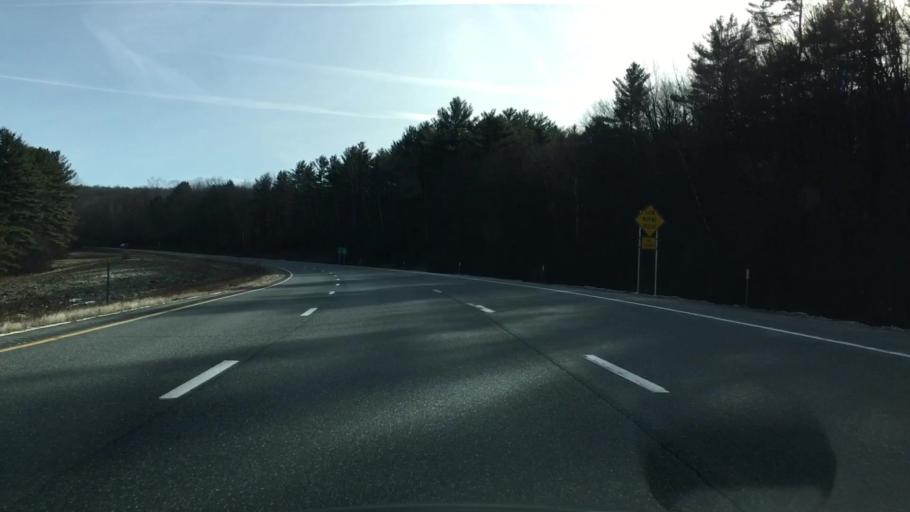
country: US
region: New Hampshire
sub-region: Grafton County
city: Lebanon
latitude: 43.6305
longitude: -72.2107
